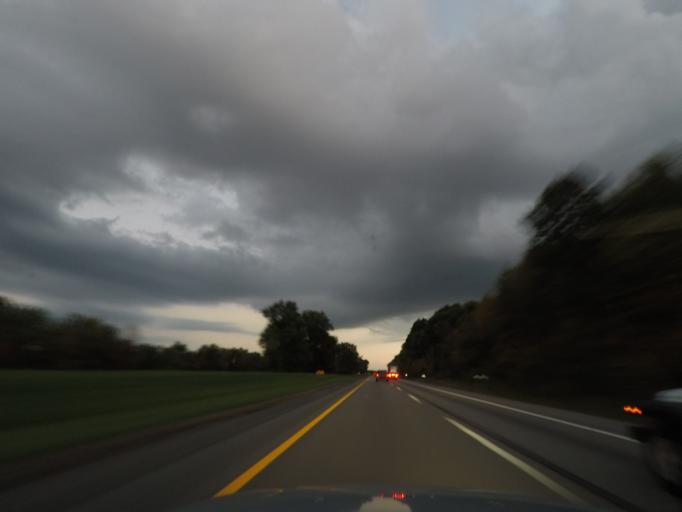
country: US
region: New York
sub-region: Ulster County
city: Plattekill
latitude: 41.6114
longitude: -74.0826
